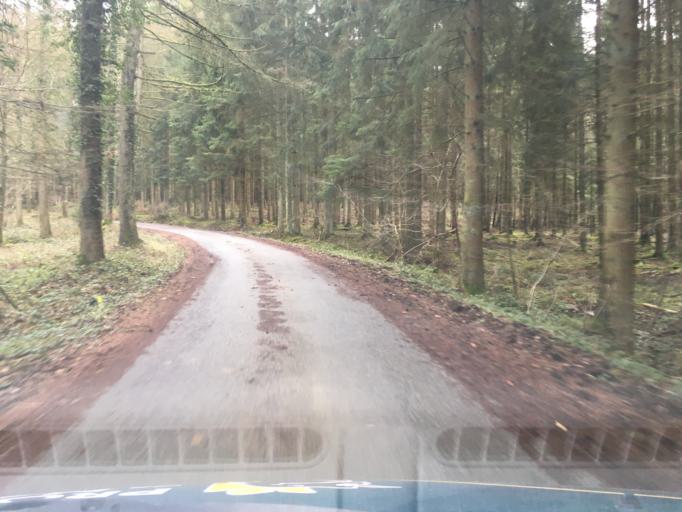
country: FR
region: Champagne-Ardenne
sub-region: Departement des Ardennes
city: Haybes
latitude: 50.0482
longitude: 4.6602
